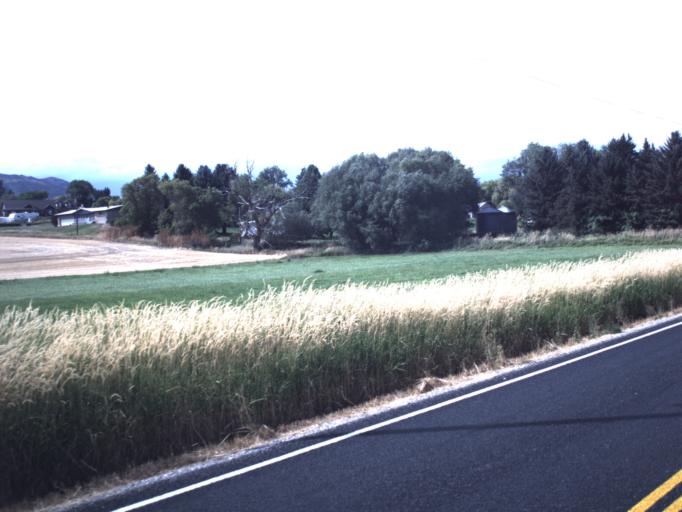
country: US
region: Utah
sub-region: Cache County
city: Benson
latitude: 41.9127
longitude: -112.0453
